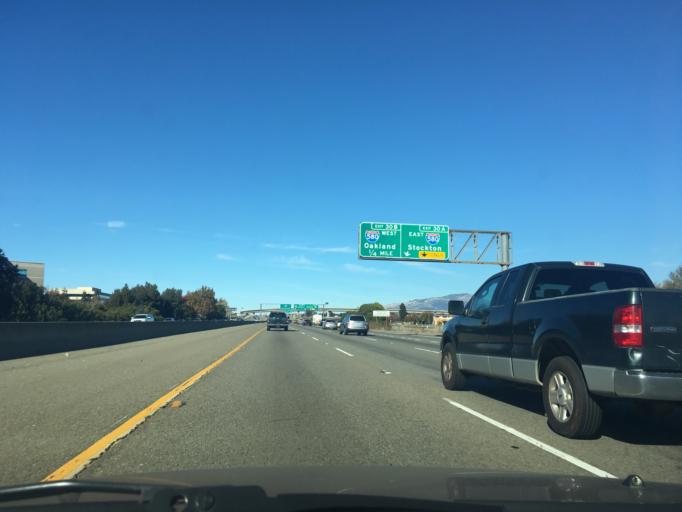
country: US
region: California
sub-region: Alameda County
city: Dublin
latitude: 37.6938
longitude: -121.9198
